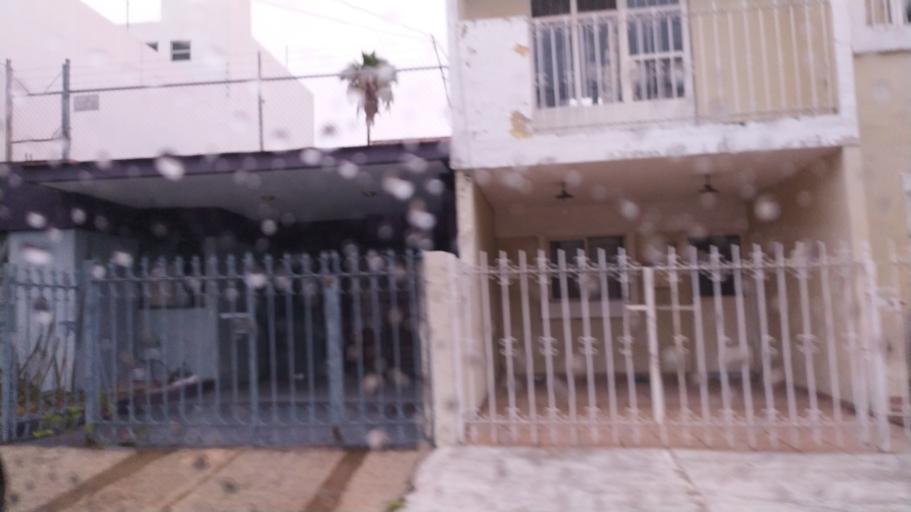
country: MX
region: Jalisco
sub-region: Zapopan
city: Zapopan
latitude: 20.7123
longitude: -103.3651
